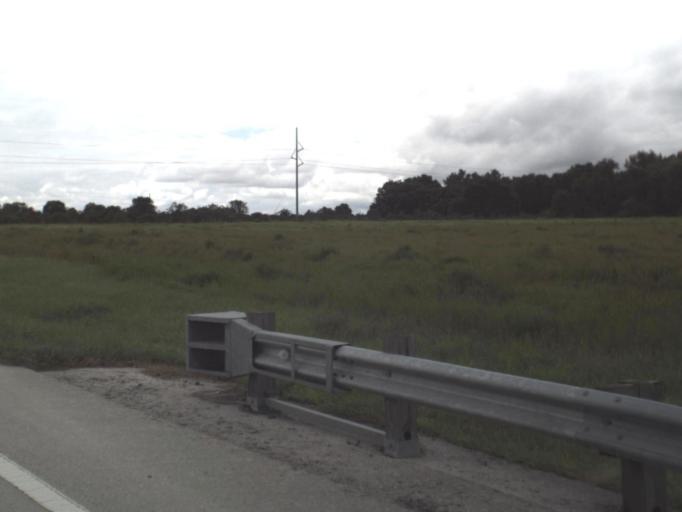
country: US
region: Florida
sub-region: Hardee County
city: Bowling Green
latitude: 27.5949
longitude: -81.8273
